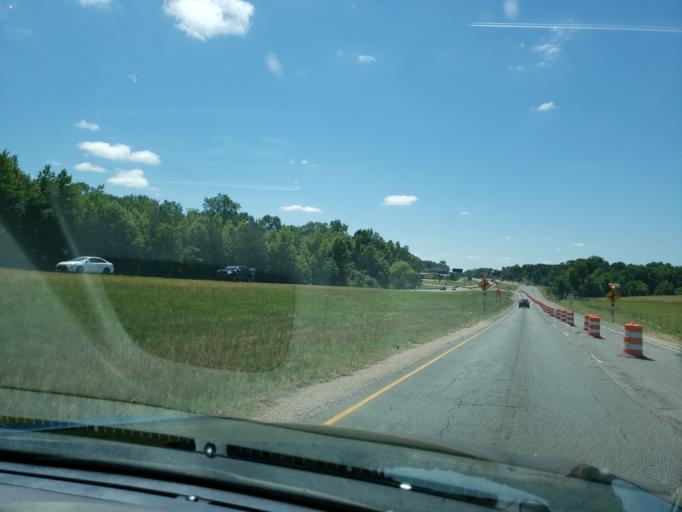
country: US
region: Alabama
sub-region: Lee County
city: Auburn
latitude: 32.6832
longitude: -85.4933
